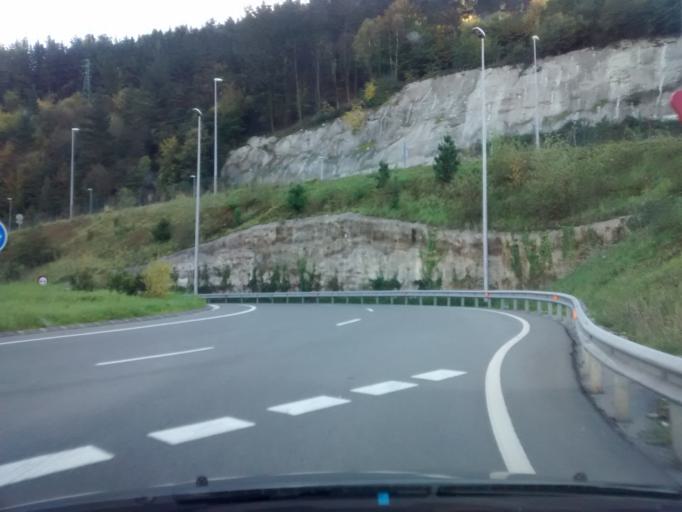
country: ES
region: Basque Country
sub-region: Bizkaia
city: Ermua
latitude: 43.1781
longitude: -2.4946
